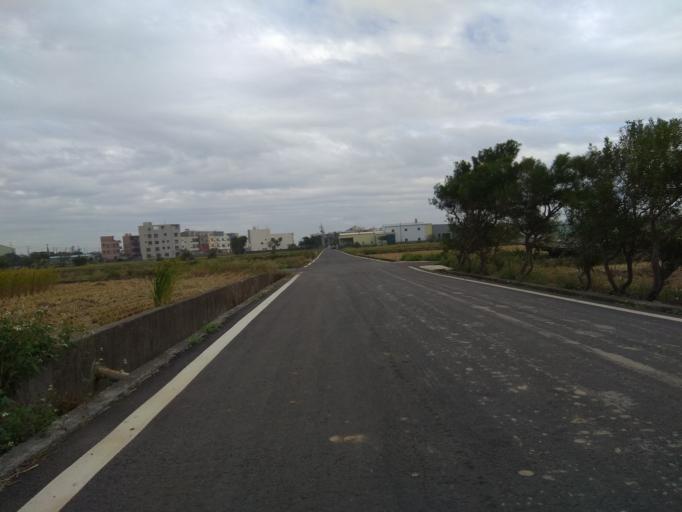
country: TW
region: Taiwan
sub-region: Hsinchu
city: Zhubei
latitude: 24.9842
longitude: 121.0494
